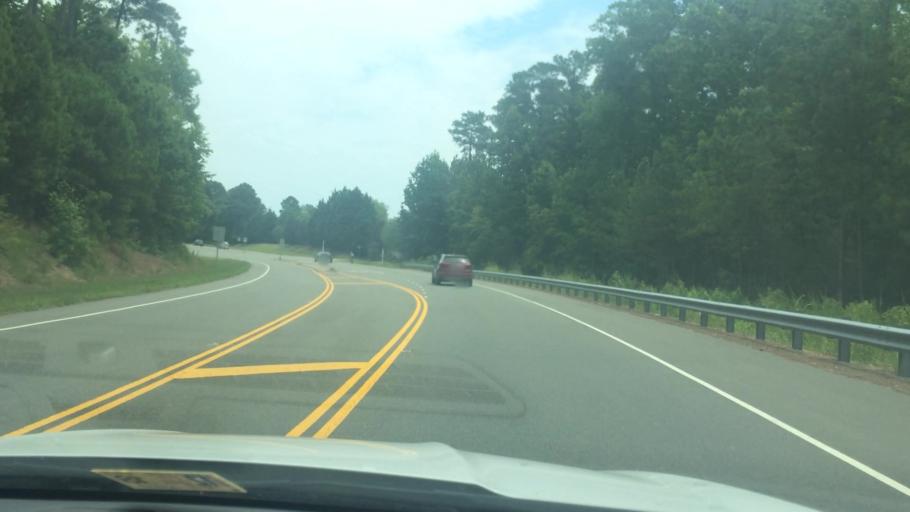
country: US
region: Virginia
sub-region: James City County
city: Williamsburg
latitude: 37.2662
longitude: -76.7680
